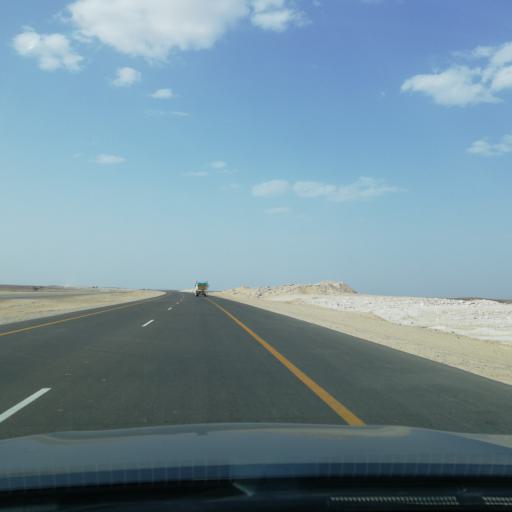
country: OM
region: Muhafazat ad Dakhiliyah
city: Adam
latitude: 22.0389
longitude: 57.5086
